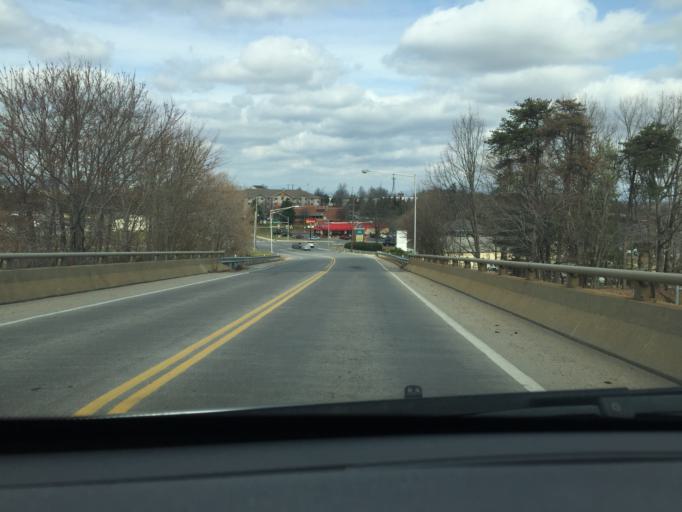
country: US
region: Virginia
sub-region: City of Lynchburg
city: West Lynchburg
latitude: 37.3564
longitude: -79.1697
